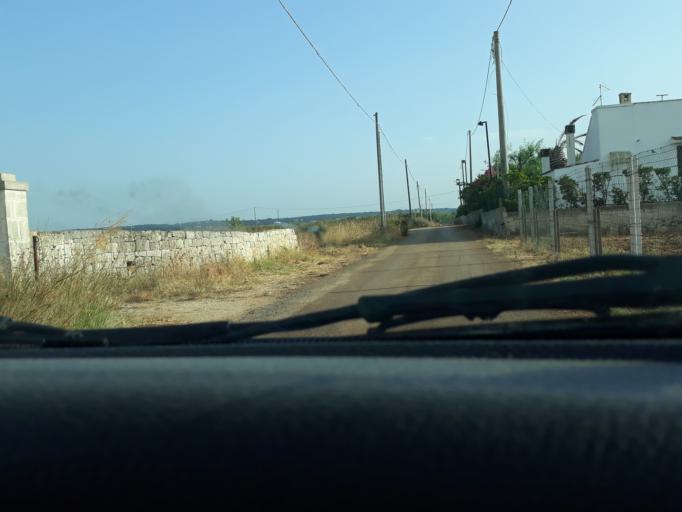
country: IT
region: Apulia
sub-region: Provincia di Brindisi
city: Carovigno
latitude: 40.7582
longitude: 17.6825
